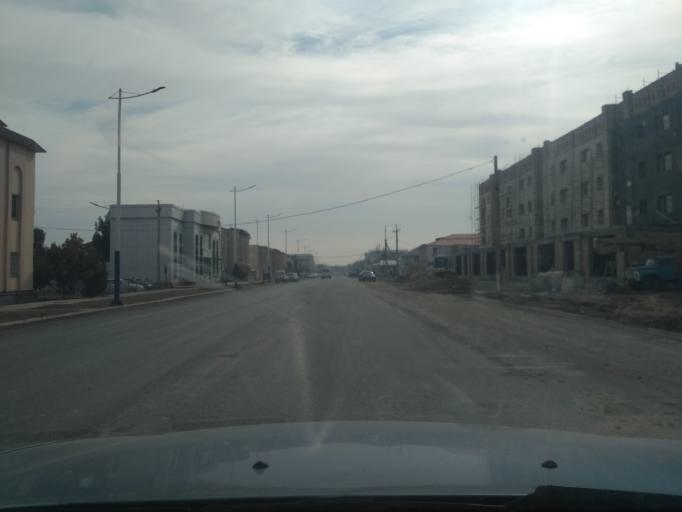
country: UZ
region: Sirdaryo
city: Guliston
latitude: 40.5017
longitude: 68.7718
